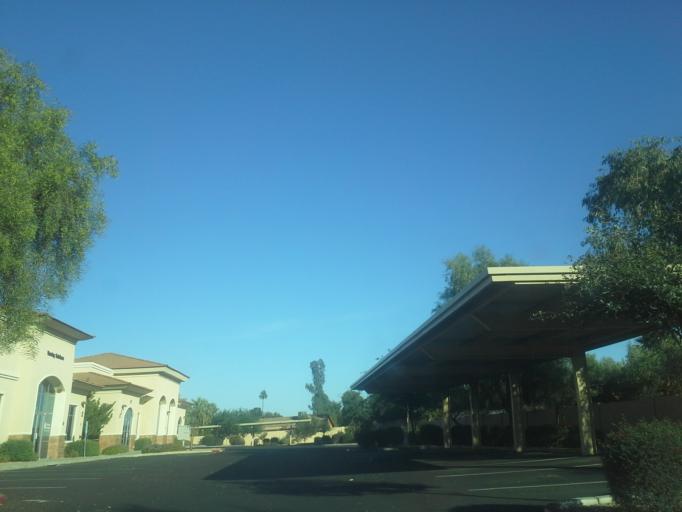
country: US
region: Arizona
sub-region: Maricopa County
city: Paradise Valley
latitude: 33.6249
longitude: -111.9951
